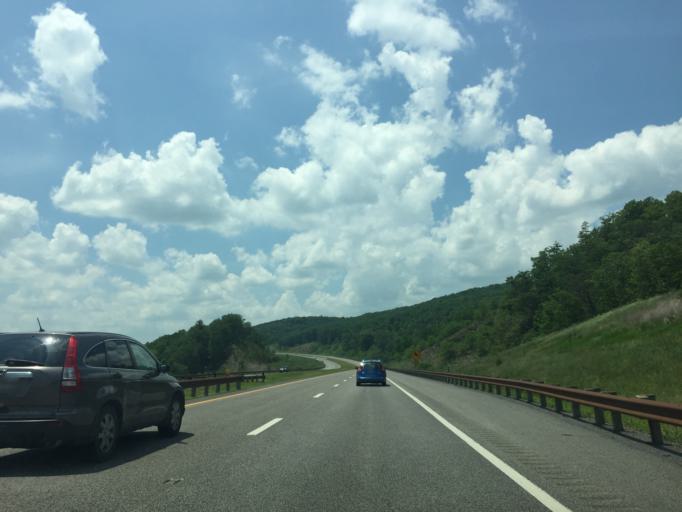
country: US
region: Virginia
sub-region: Shenandoah County
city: Woodstock
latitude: 39.0660
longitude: -78.6643
